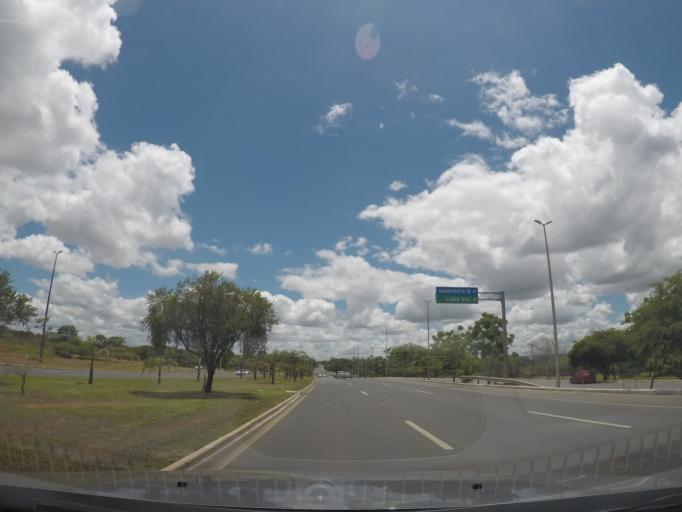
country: BR
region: Federal District
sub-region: Brasilia
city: Brasilia
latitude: -15.8446
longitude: -47.9405
